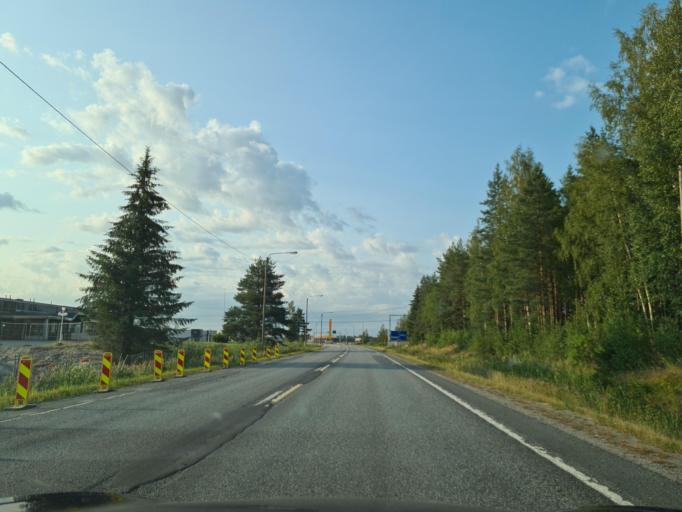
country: FI
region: Southern Ostrobothnia
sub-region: Seinaejoki
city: Kauhava
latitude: 63.0842
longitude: 23.0590
